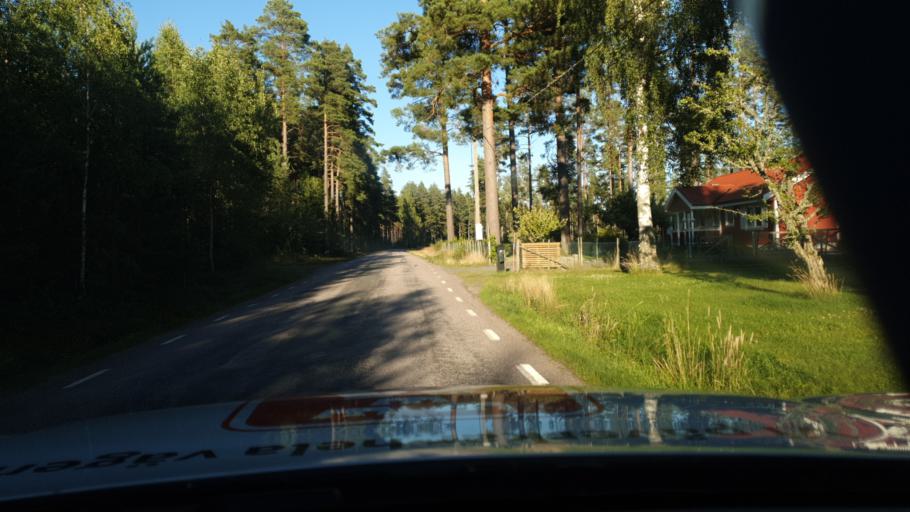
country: SE
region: Vaestra Goetaland
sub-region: Skovde Kommun
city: Stopen
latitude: 58.4529
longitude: 14.0032
